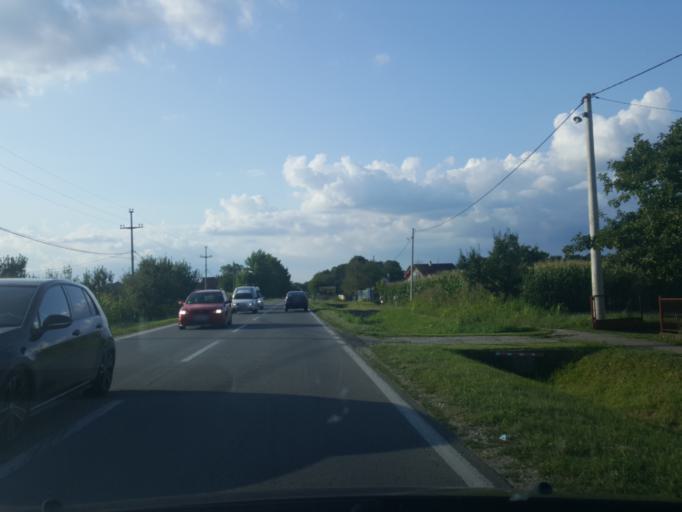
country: RS
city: Lipnicki Sor
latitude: 44.5968
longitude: 19.2562
